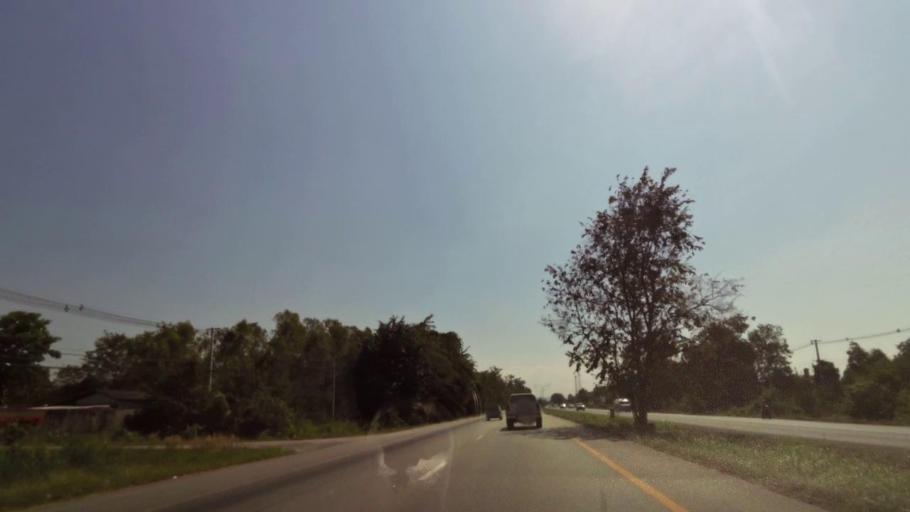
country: TH
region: Nakhon Sawan
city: Kao Liao
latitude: 15.8147
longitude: 100.1197
